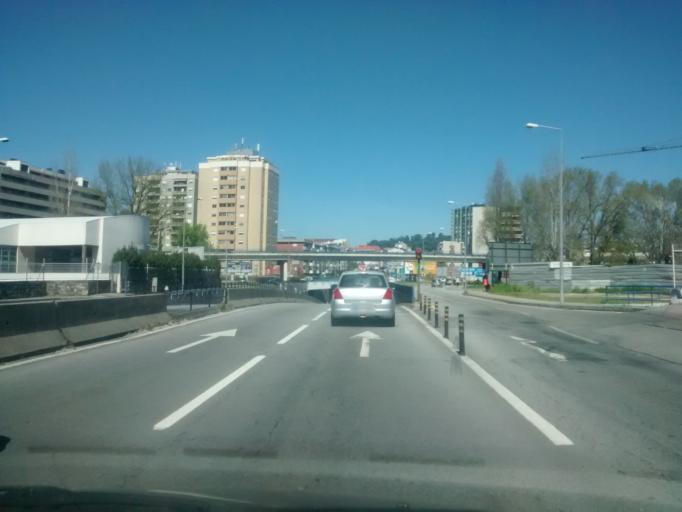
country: PT
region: Braga
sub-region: Braga
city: Braga
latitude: 41.5513
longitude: -8.4062
